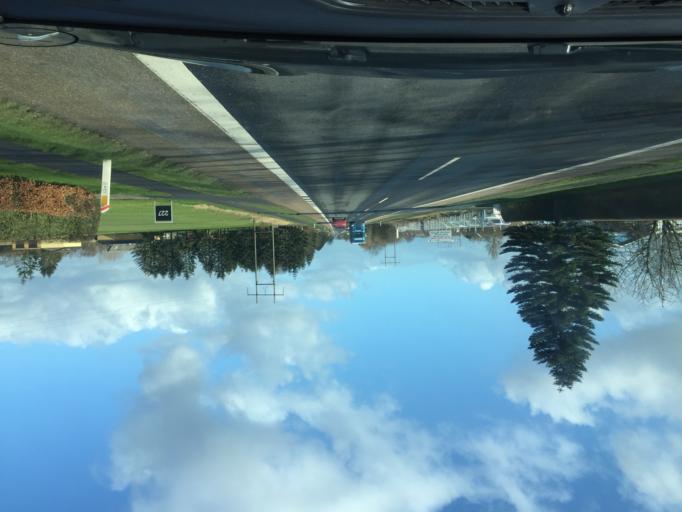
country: DK
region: South Denmark
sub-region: Middelfart Kommune
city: Norre Aby
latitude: 55.4725
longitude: 9.8809
